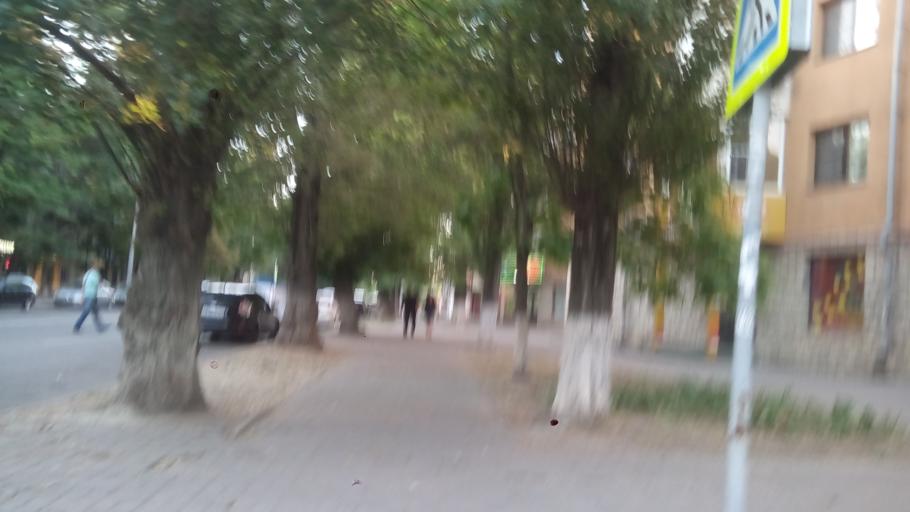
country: RU
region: Rostov
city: Imeni Chkalova
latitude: 47.2521
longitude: 39.7696
